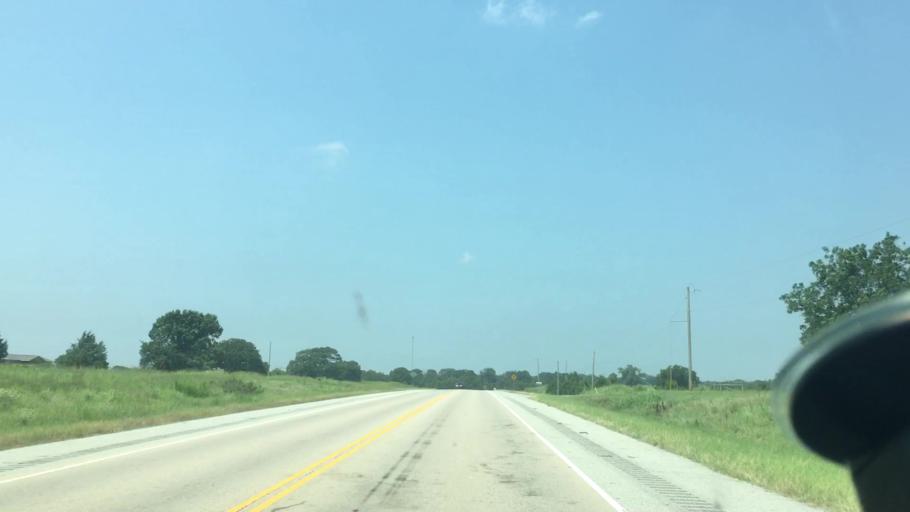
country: US
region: Oklahoma
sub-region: Atoka County
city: Atoka
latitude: 34.2886
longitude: -95.9648
